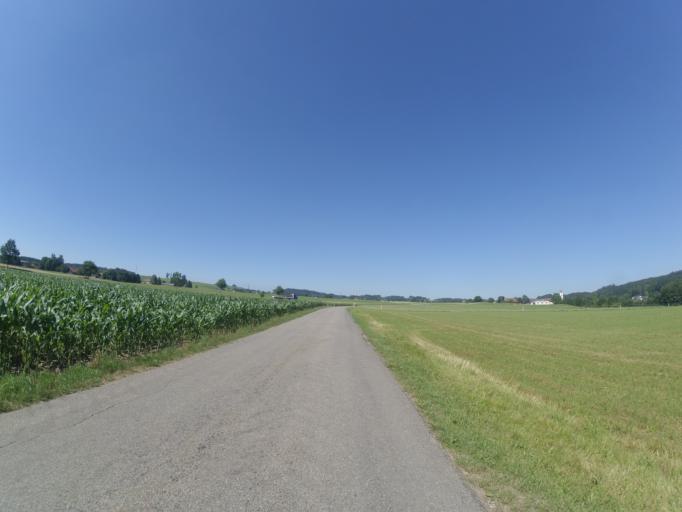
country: DE
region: Baden-Wuerttemberg
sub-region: Tuebingen Region
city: Leutkirch im Allgau
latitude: 47.8443
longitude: 9.9801
